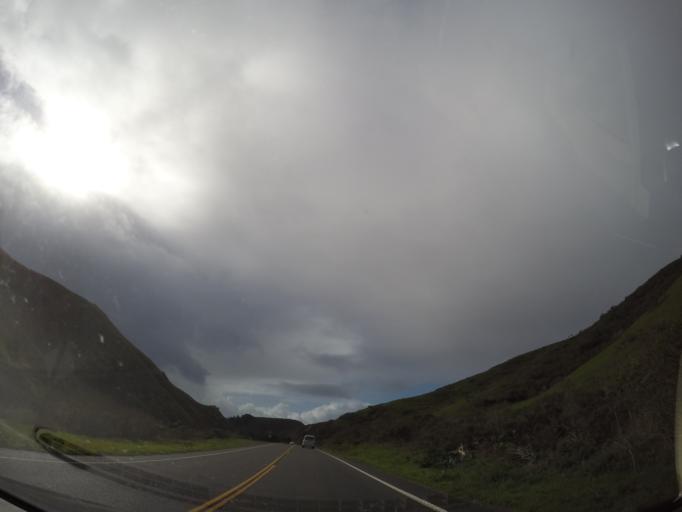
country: US
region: California
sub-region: Sonoma County
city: Bodega Bay
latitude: 38.3267
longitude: -123.0072
